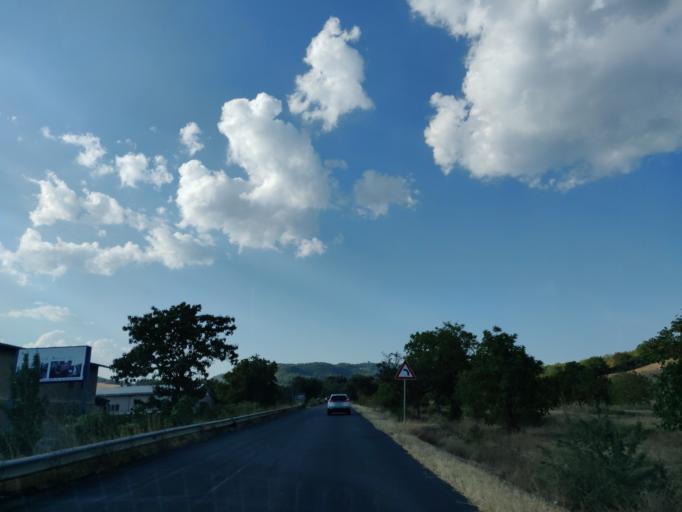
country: IT
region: Latium
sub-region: Provincia di Viterbo
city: Acquapendente
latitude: 42.7689
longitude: 11.8558
